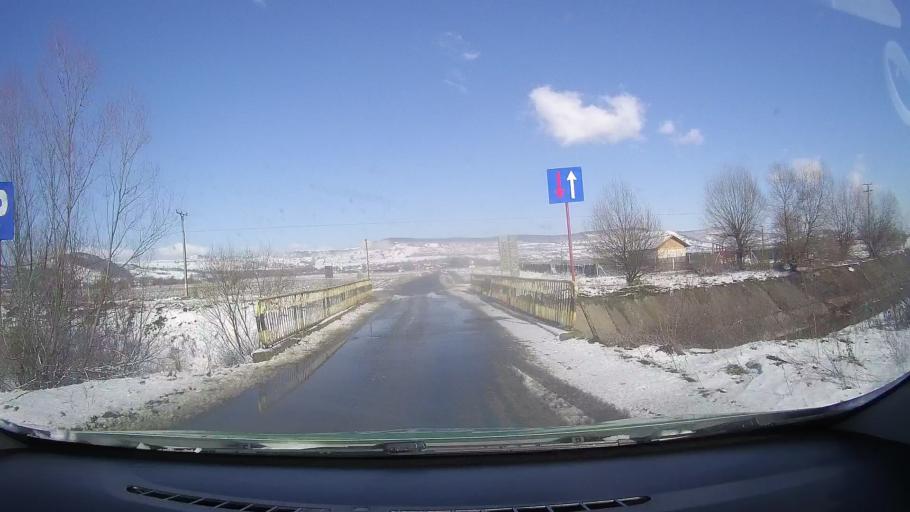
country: RO
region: Sibiu
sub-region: Comuna Avrig
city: Avrig
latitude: 45.7462
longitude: 24.3917
